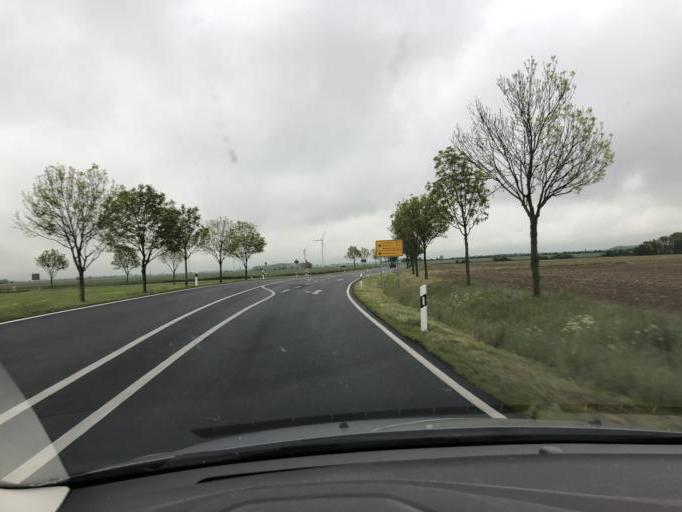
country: DE
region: Saxony
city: Dobernitz
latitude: 51.5141
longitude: 12.3692
